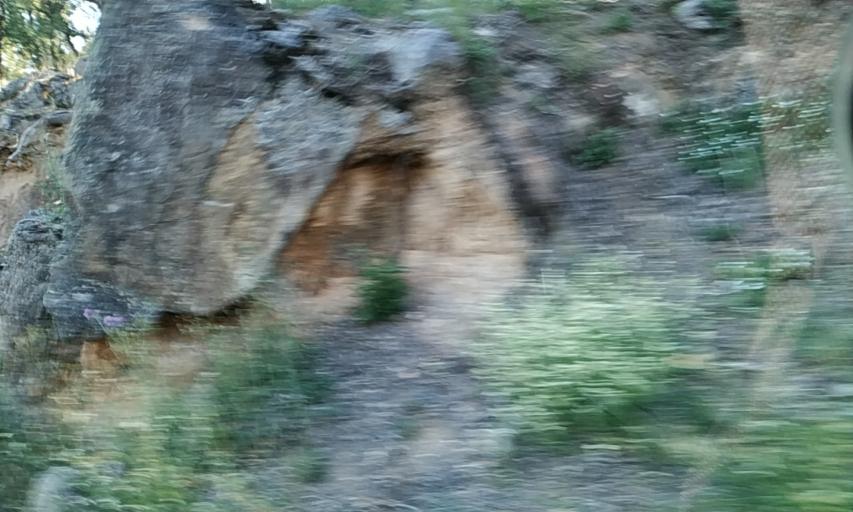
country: PT
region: Portalegre
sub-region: Portalegre
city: Portalegre
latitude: 39.3315
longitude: -7.4238
